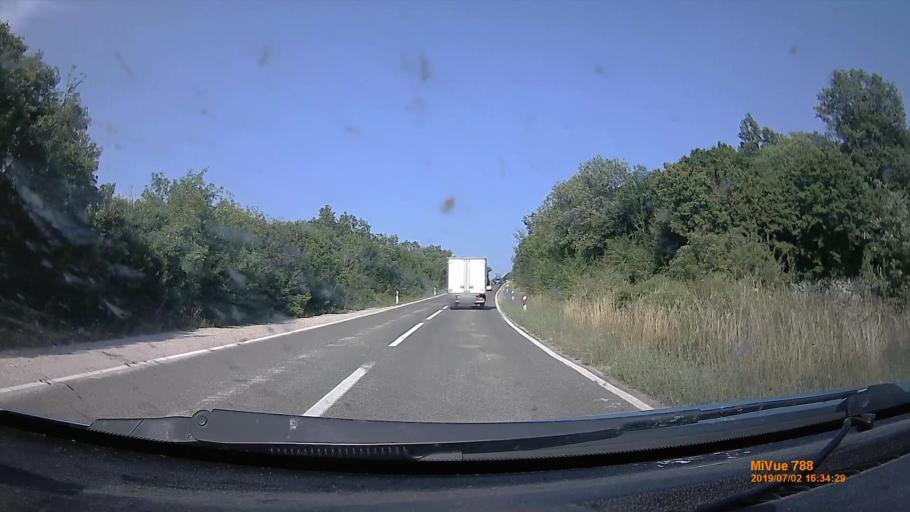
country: HR
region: Primorsko-Goranska
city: Njivice
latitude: 45.0820
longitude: 14.5023
